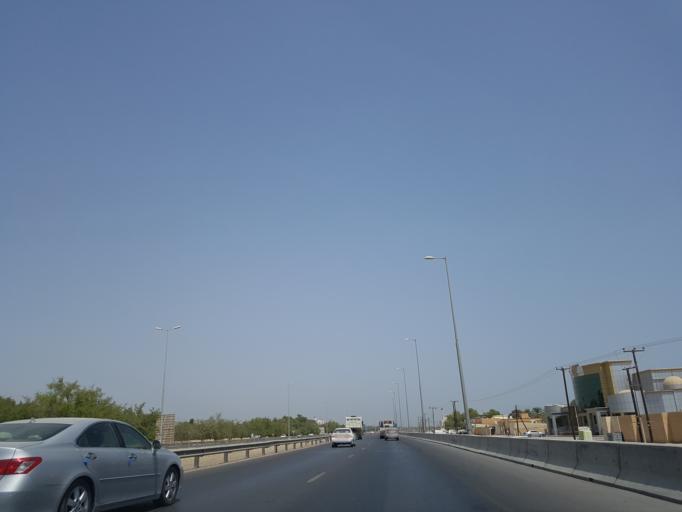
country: OM
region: Al Batinah
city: Saham
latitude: 24.1494
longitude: 56.8703
